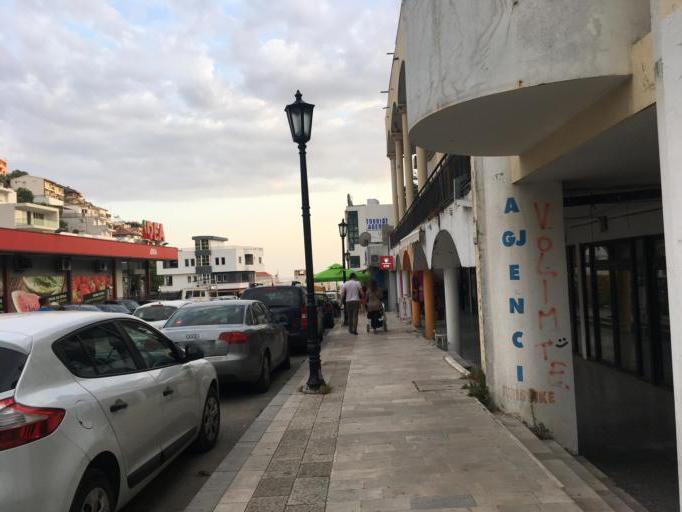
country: ME
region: Ulcinj
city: Ulcinj
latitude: 41.9277
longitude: 19.2060
